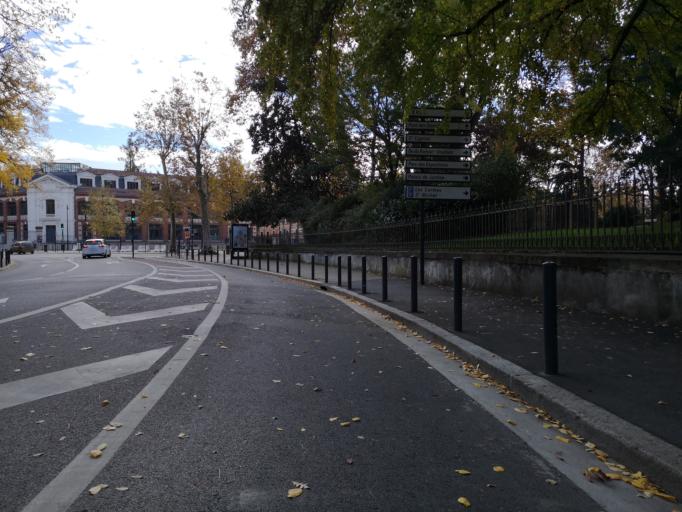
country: FR
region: Midi-Pyrenees
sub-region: Departement de la Haute-Garonne
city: Toulouse
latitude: 43.5960
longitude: 1.4510
